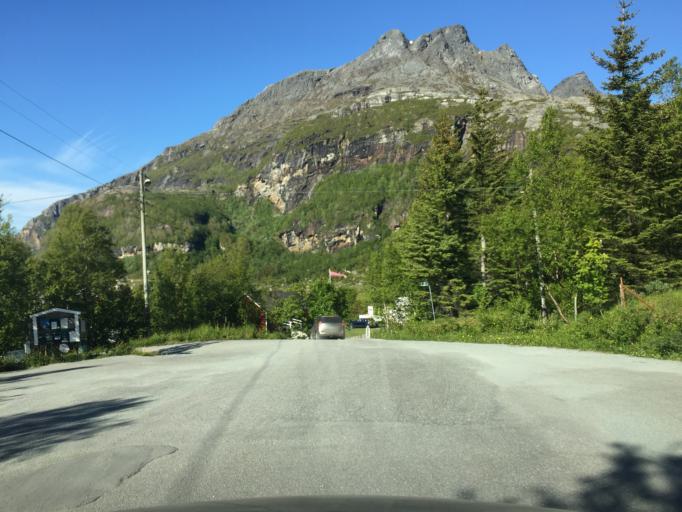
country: NO
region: Nordland
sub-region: Bodo
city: Loding
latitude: 67.4084
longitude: 14.6271
